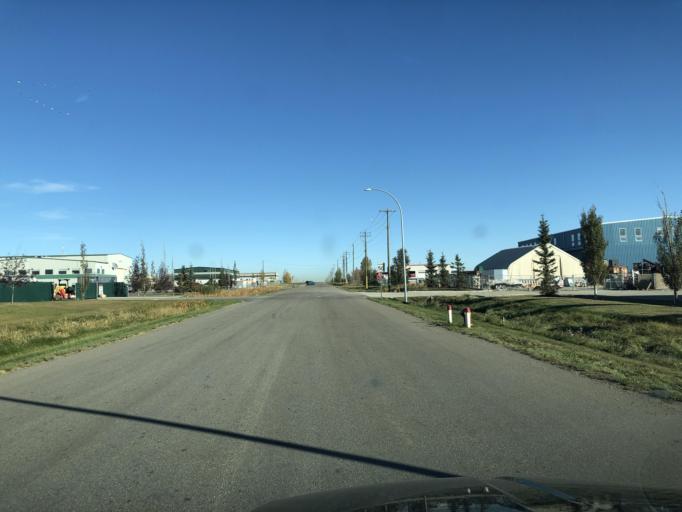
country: CA
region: Alberta
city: Chestermere
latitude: 50.9627
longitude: -113.9026
